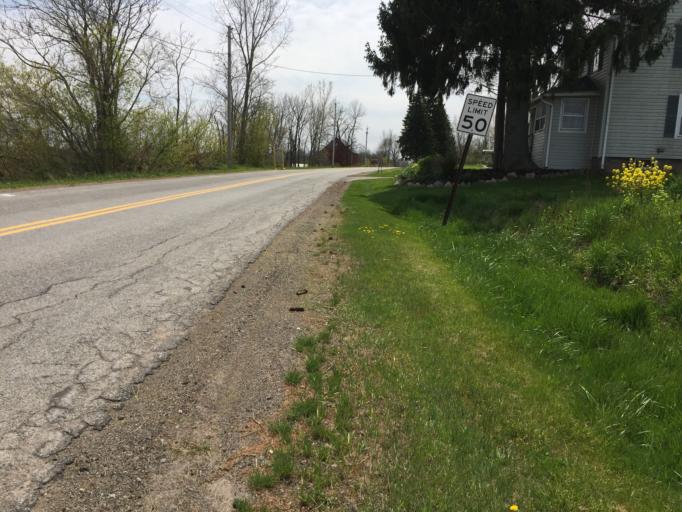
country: US
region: New York
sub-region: Wayne County
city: Marion
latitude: 43.1504
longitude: -77.1704
